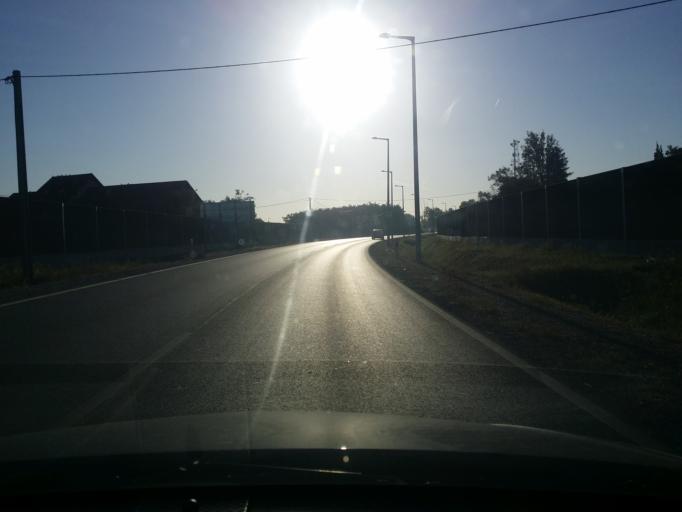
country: HU
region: Bacs-Kiskun
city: Kecskemet
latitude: 46.9057
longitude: 19.7441
